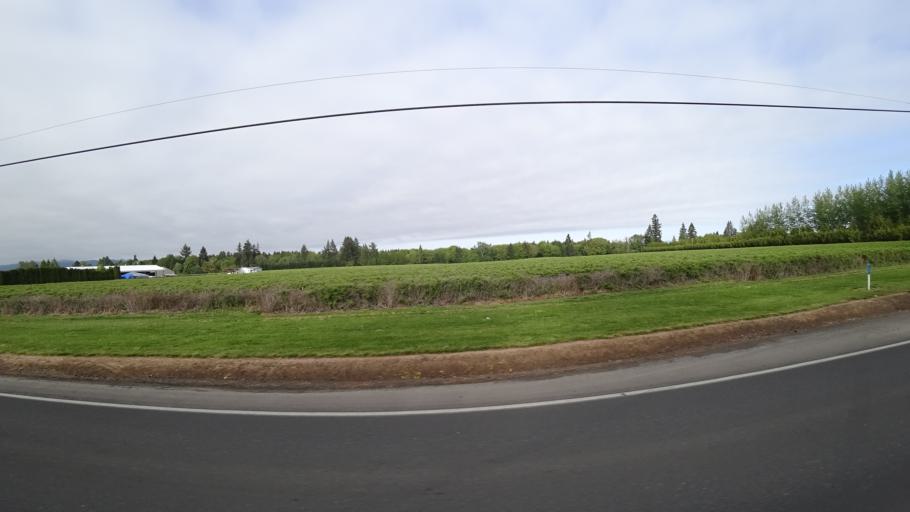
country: US
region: Oregon
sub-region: Washington County
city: Hillsboro
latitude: 45.4934
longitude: -122.9912
